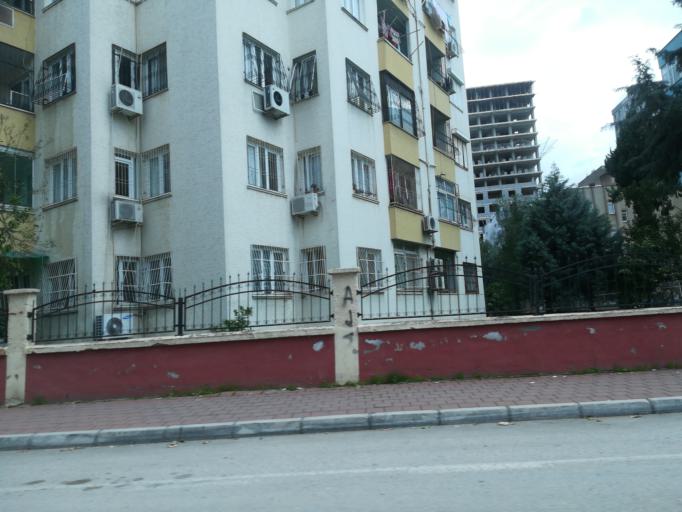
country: TR
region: Adana
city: Adana
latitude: 37.0380
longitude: 35.3128
